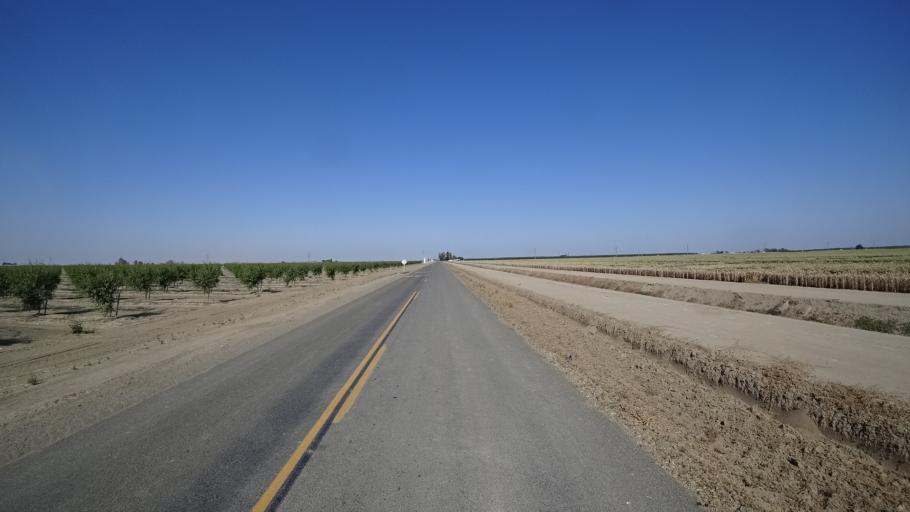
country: US
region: California
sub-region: Kings County
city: Home Garden
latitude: 36.2405
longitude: -119.5839
